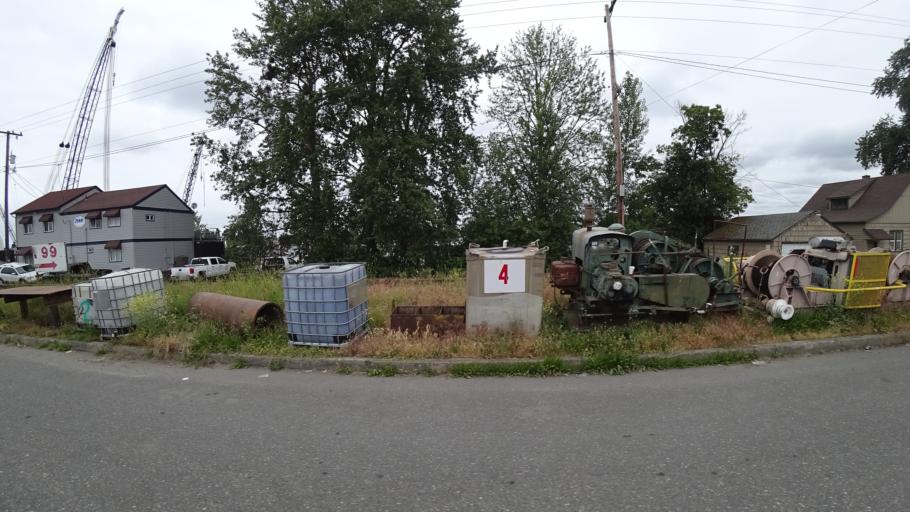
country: US
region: Washington
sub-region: Clark County
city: Vancouver
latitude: 45.6066
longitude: -122.6839
